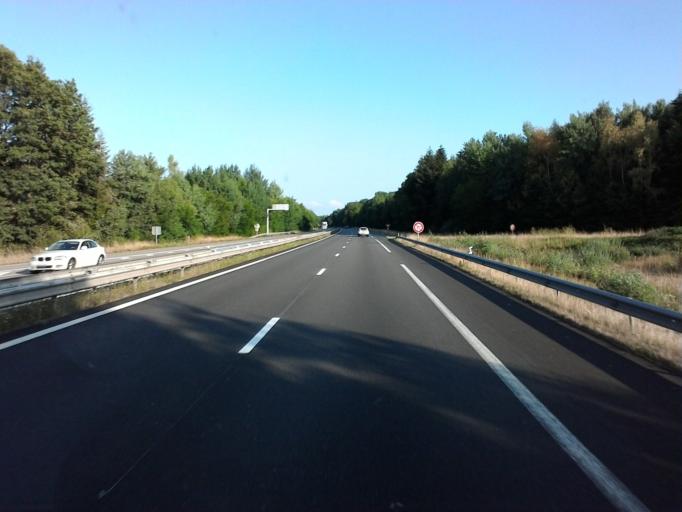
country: FR
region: Lorraine
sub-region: Departement des Vosges
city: Thaon-les-Vosges
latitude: 48.2523
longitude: 6.3977
